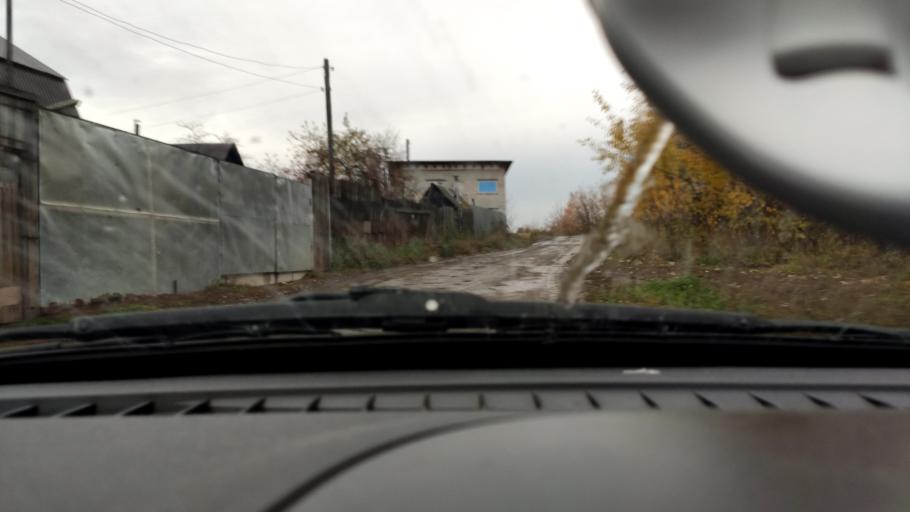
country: RU
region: Perm
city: Kondratovo
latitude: 57.9552
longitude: 56.1608
